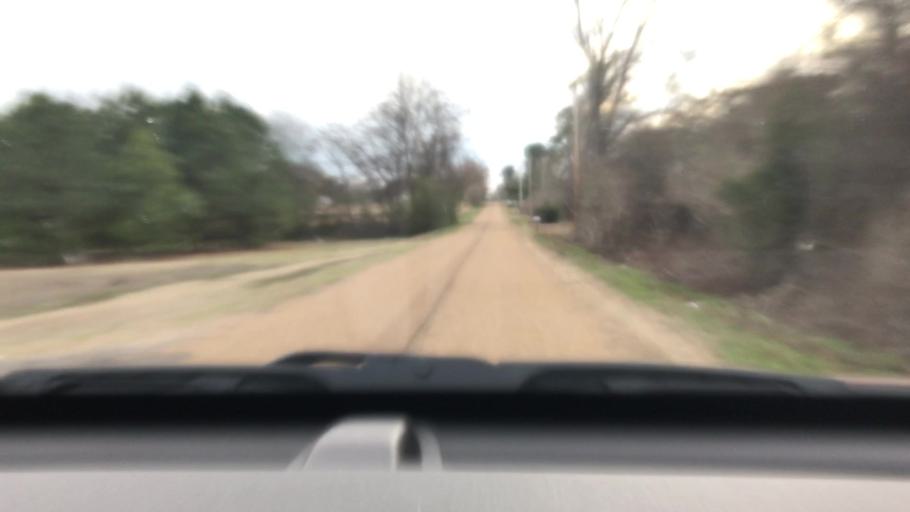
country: US
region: Arkansas
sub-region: Hempstead County
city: Hope
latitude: 33.6385
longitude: -93.5603
